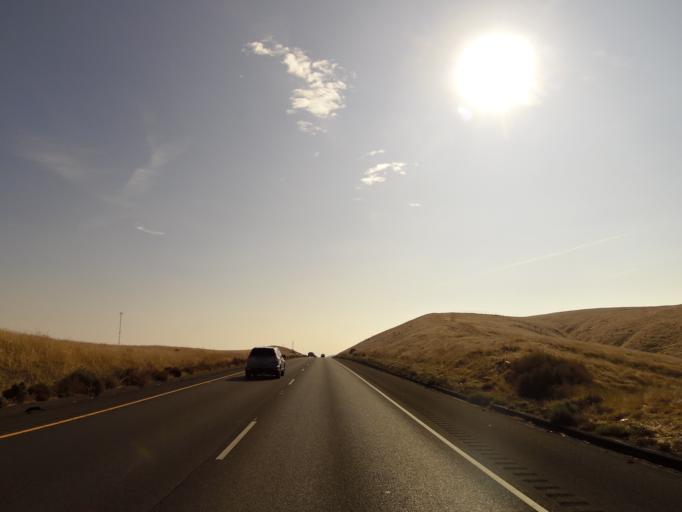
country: US
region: California
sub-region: Kings County
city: Kettleman City
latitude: 35.9989
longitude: -119.9783
